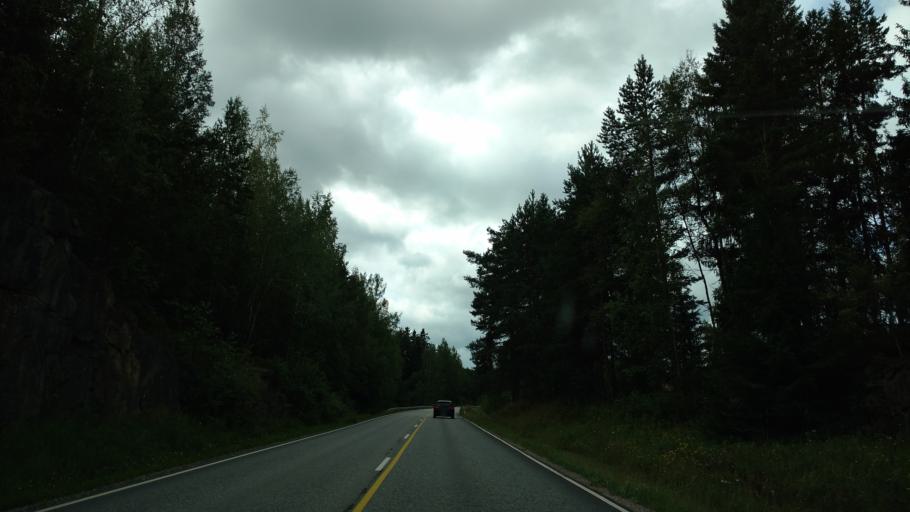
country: FI
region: Varsinais-Suomi
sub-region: Aboland-Turunmaa
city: Kimito
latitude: 60.1415
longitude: 22.6762
